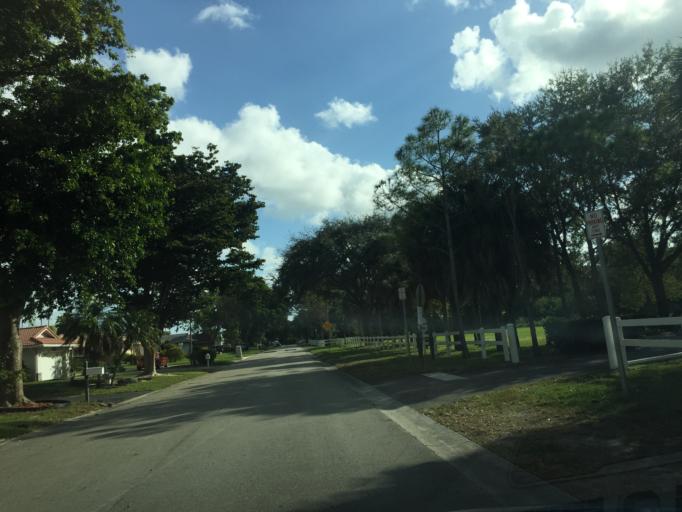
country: US
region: Florida
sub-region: Broward County
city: Tamarac
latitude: 26.2322
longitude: -80.2470
